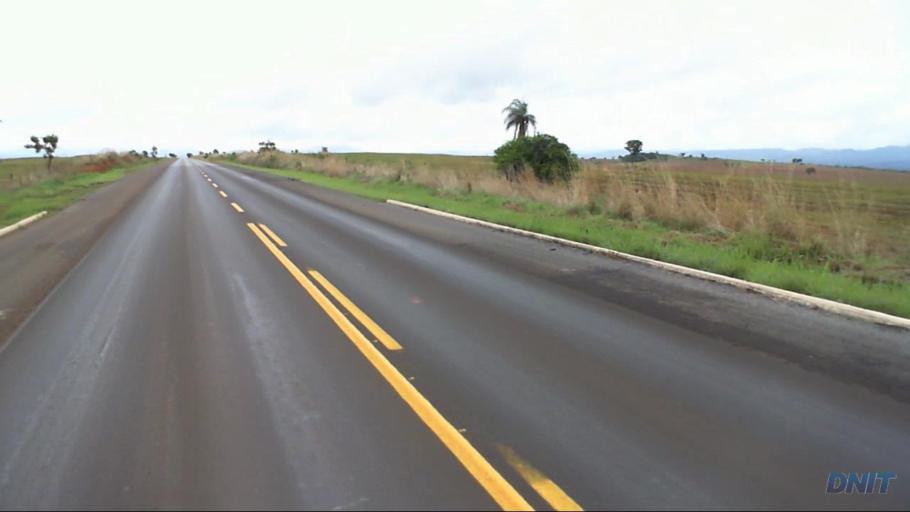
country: BR
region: Goias
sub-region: Padre Bernardo
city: Padre Bernardo
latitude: -15.2110
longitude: -48.4874
